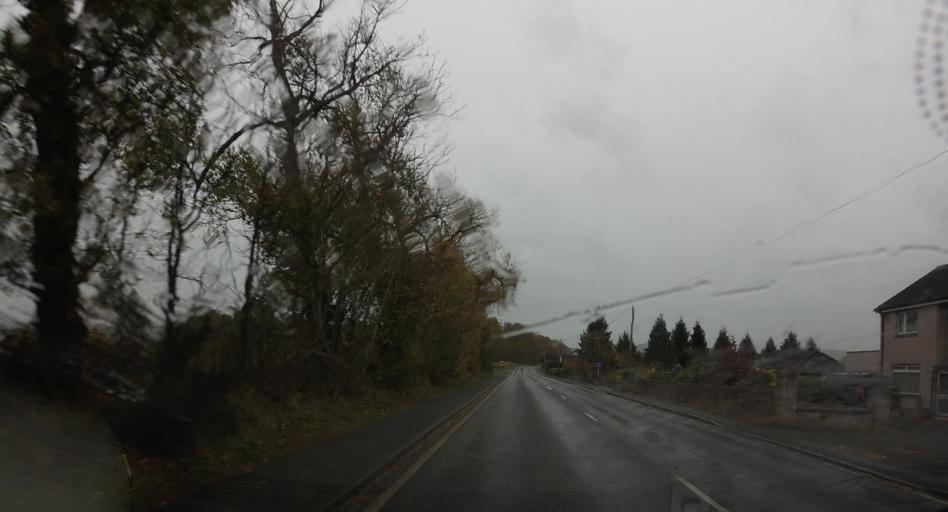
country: GB
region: Scotland
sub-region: Perth and Kinross
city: Coupar Angus
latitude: 56.5355
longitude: -3.2501
